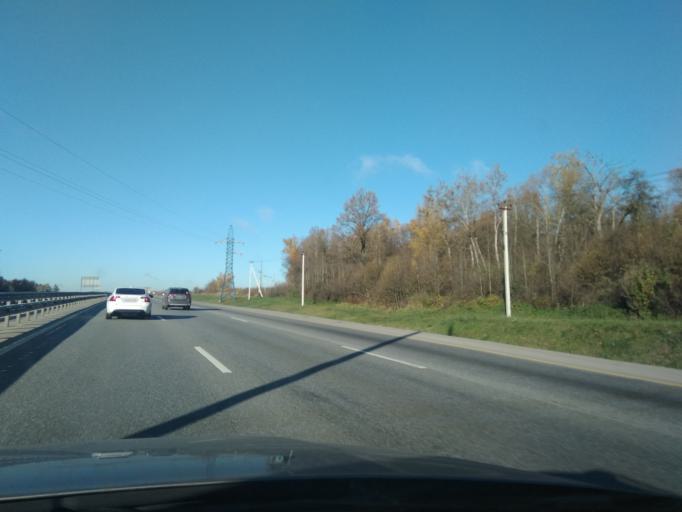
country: RU
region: Moskovskaya
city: Yershovo
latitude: 55.8263
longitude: 36.9009
